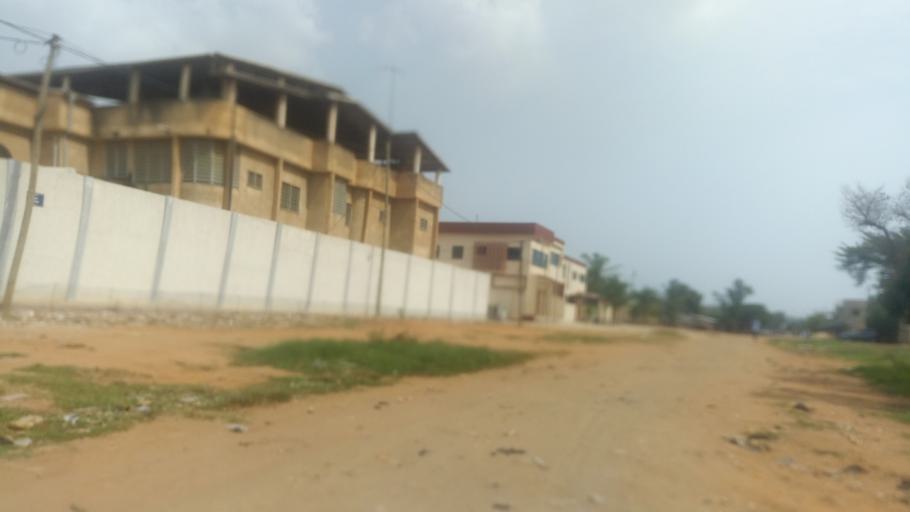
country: TG
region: Maritime
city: Lome
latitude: 6.1748
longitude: 1.1876
